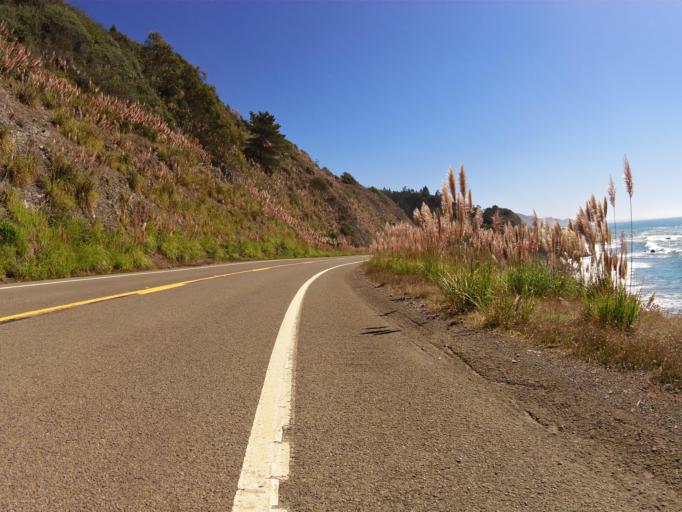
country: US
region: California
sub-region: Mendocino County
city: Fort Bragg
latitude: 39.7064
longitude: -123.8049
